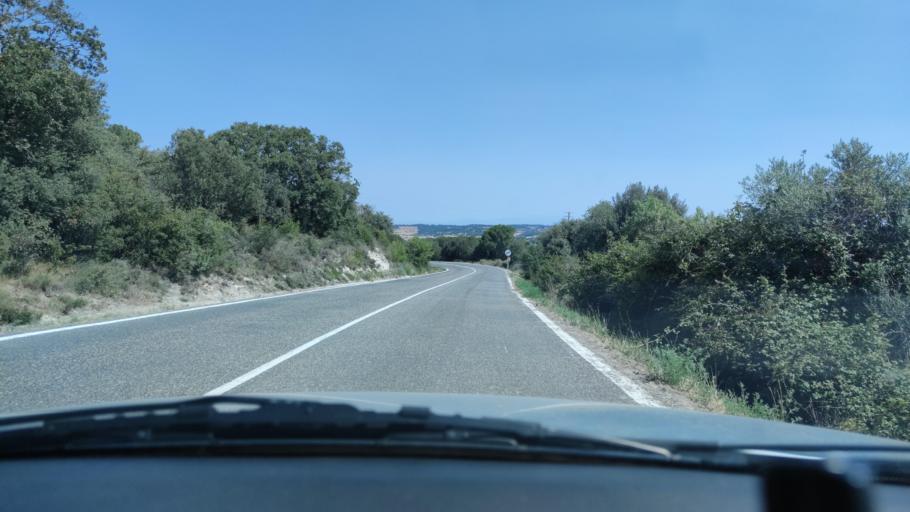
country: ES
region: Catalonia
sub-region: Provincia de Tarragona
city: Santa Coloma de Queralt
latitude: 41.6017
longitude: 1.3478
